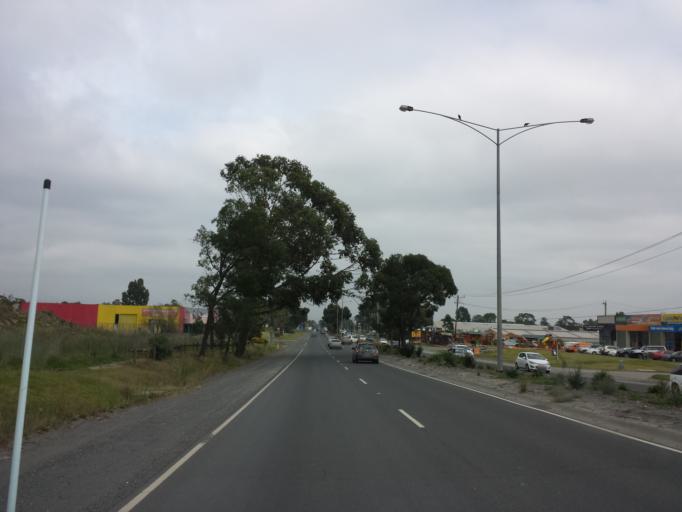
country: AU
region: Victoria
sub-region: Maroondah
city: Kilsyth South
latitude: -37.8167
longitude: 145.3223
